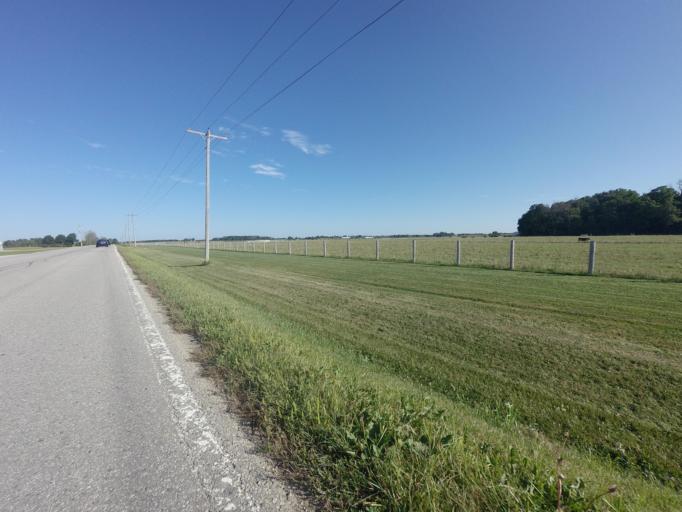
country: CA
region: Ontario
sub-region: Wellington County
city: Guelph
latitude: 43.6465
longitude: -80.4100
